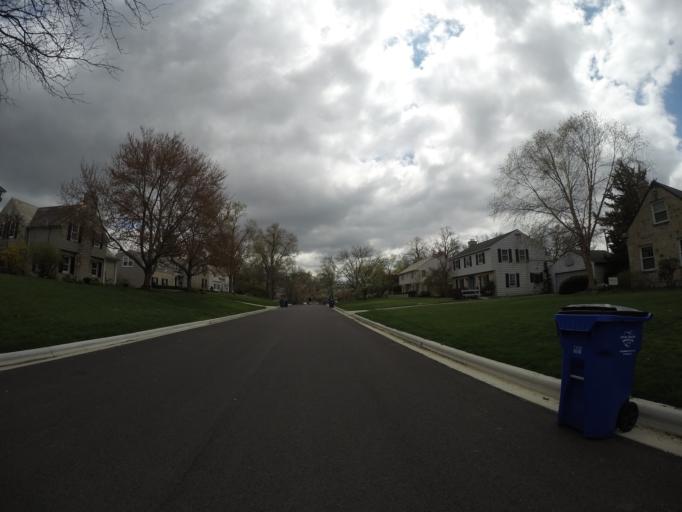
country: US
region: Ohio
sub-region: Franklin County
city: Upper Arlington
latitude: 39.9985
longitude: -83.0672
